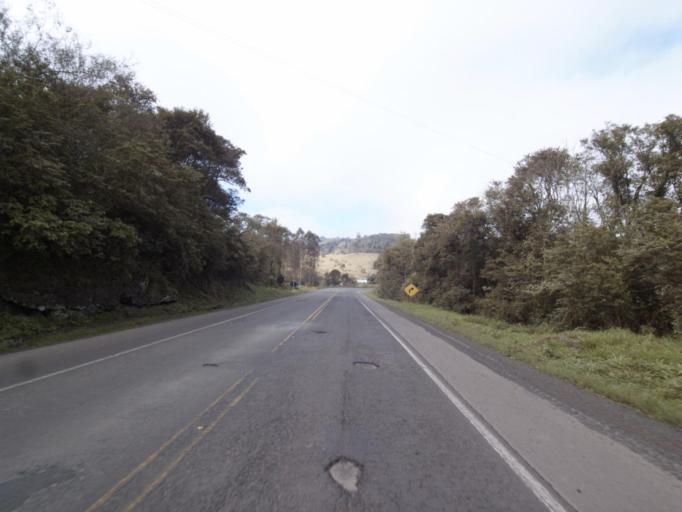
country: BR
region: Rio Grande do Sul
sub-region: Frederico Westphalen
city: Frederico Westphalen
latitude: -27.0196
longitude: -53.2299
